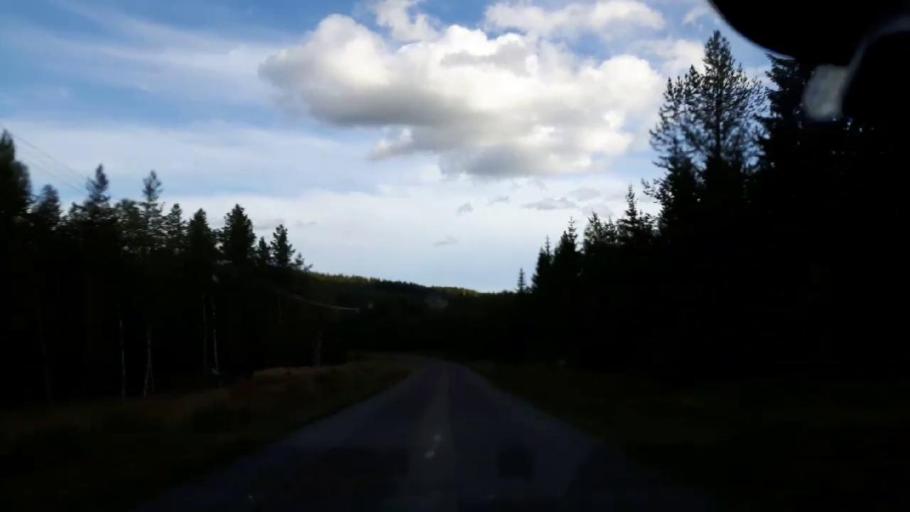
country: SE
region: Jaemtland
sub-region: Ragunda Kommun
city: Hammarstrand
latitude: 63.4231
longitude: 16.0634
